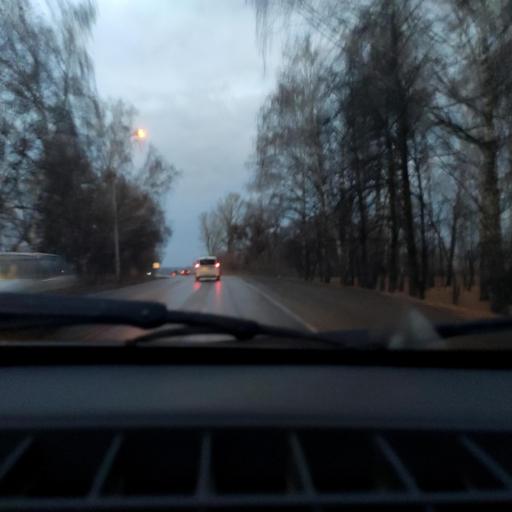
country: RU
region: Bashkortostan
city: Avdon
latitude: 54.7195
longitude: 55.8086
